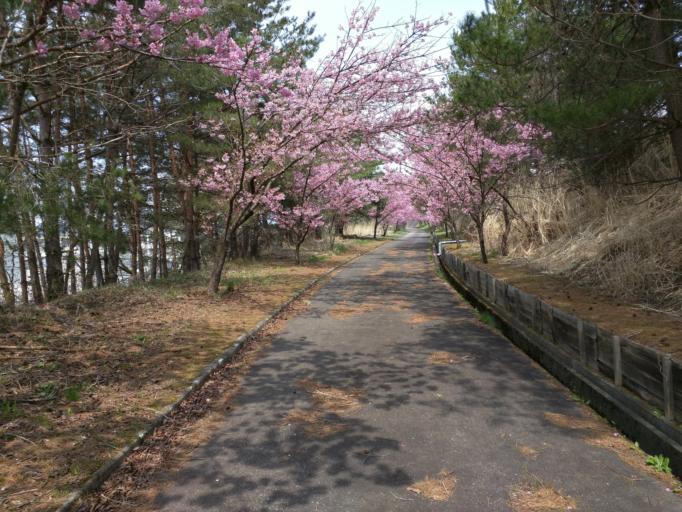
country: JP
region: Fukushima
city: Kitakata
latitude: 37.5292
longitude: 139.9593
